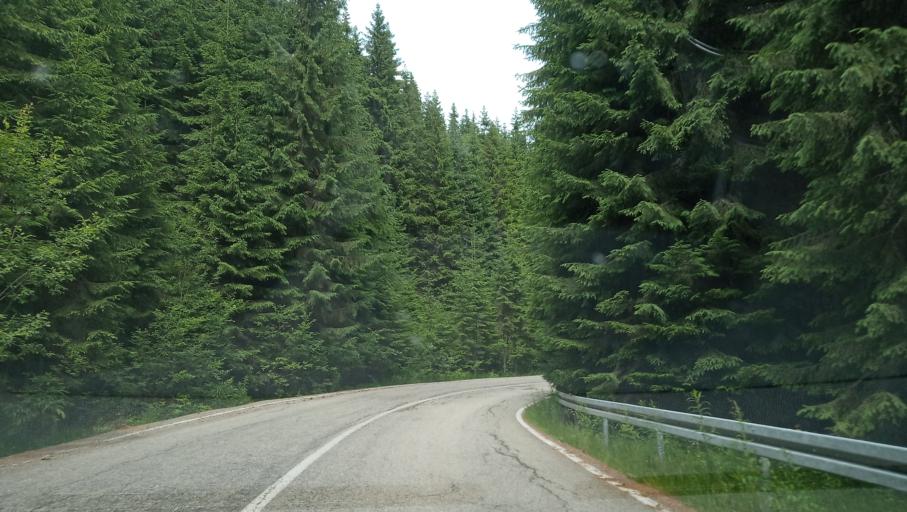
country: RO
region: Valcea
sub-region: Comuna Voineasa
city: Voineasa
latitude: 45.4263
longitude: 23.7462
